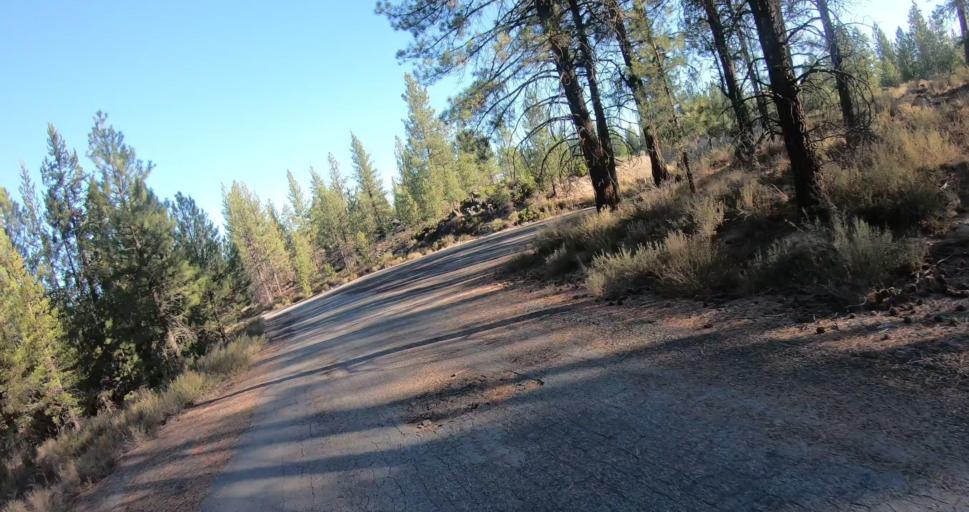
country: US
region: Oregon
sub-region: Deschutes County
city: La Pine
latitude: 43.7196
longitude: -121.4228
